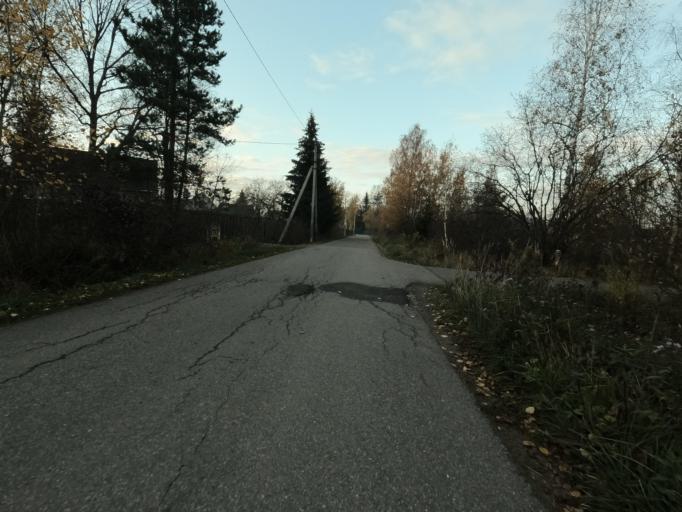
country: RU
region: Leningrad
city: Mga
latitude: 59.7792
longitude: 31.2045
